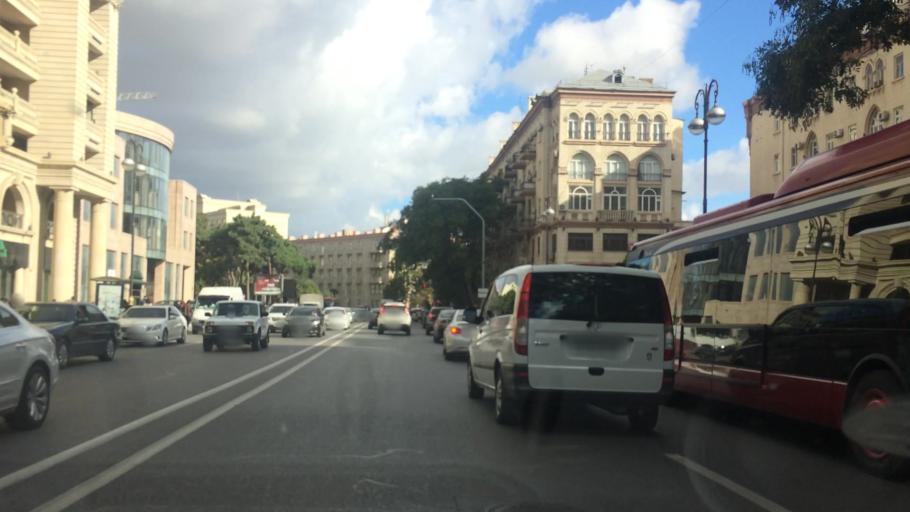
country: AZ
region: Baki
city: Badamdar
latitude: 40.3849
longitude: 49.8238
